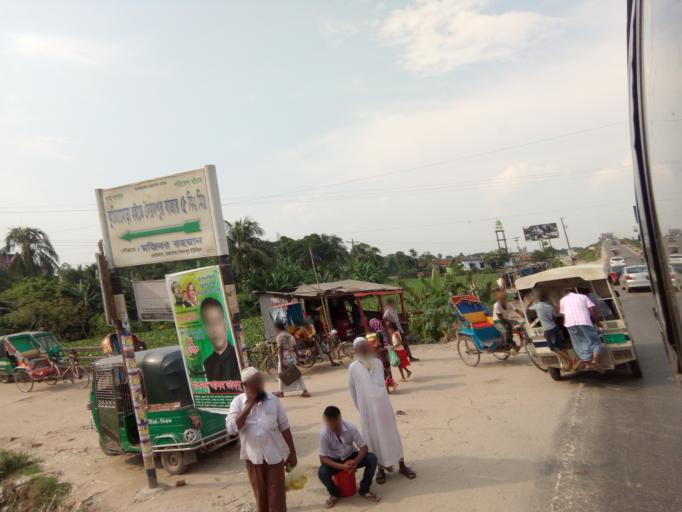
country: BD
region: Dhaka
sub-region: Dhaka
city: Dhaka
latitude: 23.6317
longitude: 90.3444
